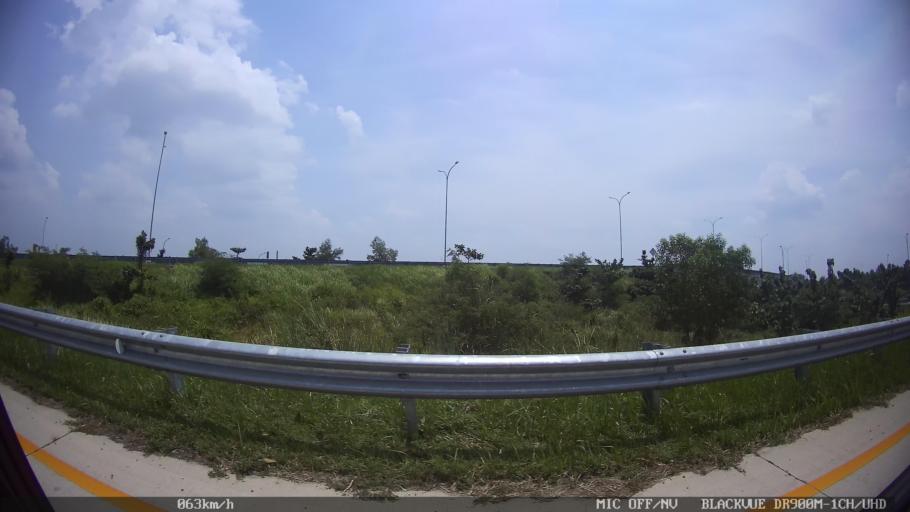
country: ID
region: Lampung
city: Natar
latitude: -5.2741
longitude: 105.2152
